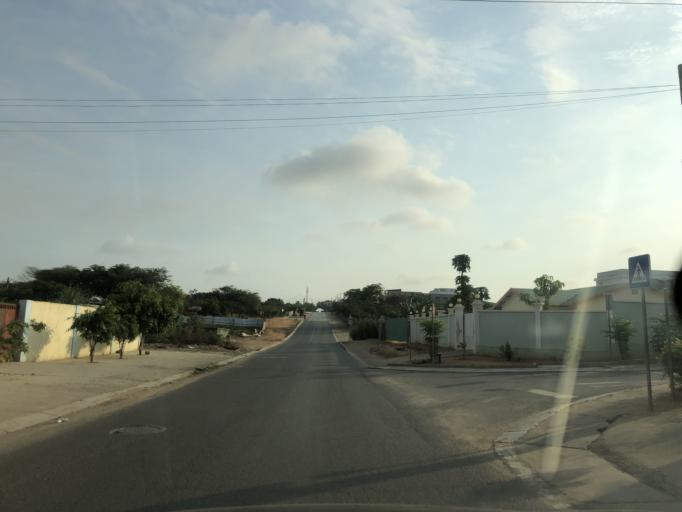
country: AO
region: Luanda
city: Luanda
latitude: -8.9034
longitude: 13.2239
